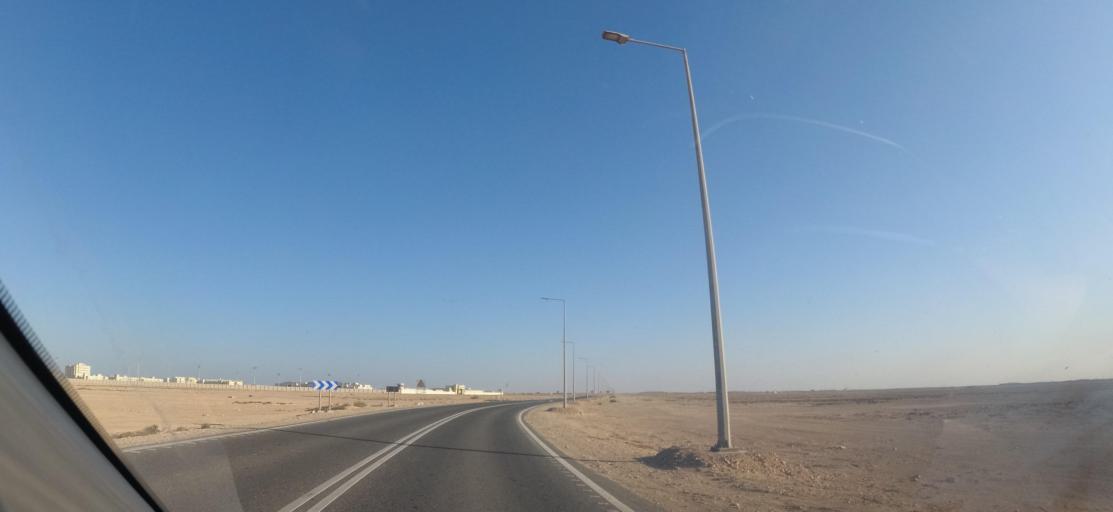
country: QA
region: Madinat ash Shamal
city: Ar Ru'ays
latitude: 26.1321
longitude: 51.2311
